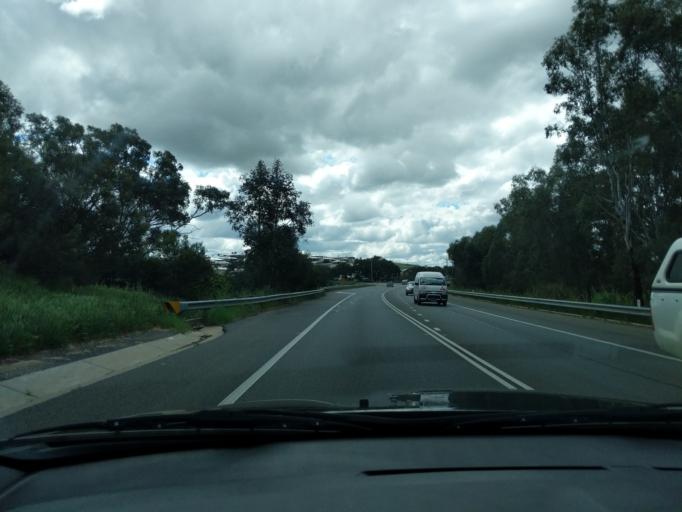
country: AU
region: New South Wales
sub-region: Wagga Wagga
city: Wagga Wagga
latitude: -35.0871
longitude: 147.3486
